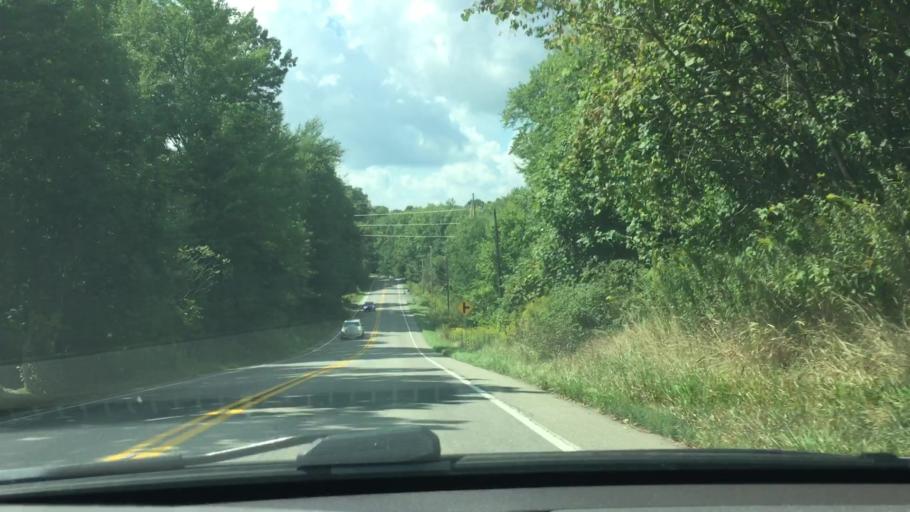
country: US
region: Pennsylvania
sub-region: Mercer County
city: Grove City
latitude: 41.1416
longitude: -80.1873
